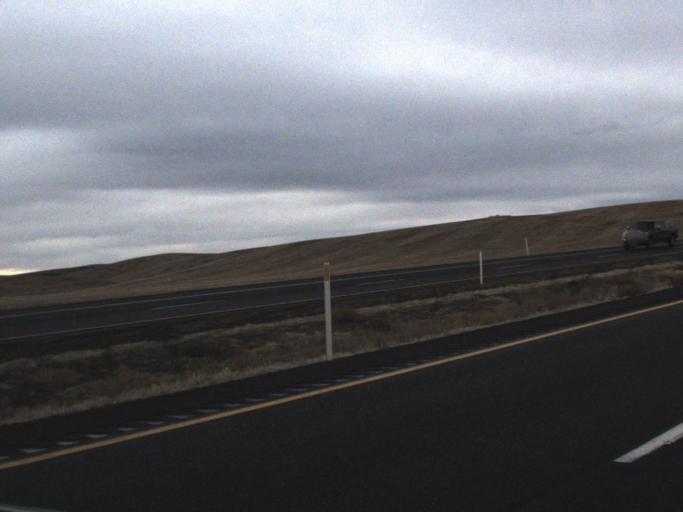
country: US
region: Washington
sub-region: Walla Walla County
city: Garrett
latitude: 46.0534
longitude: -118.4693
